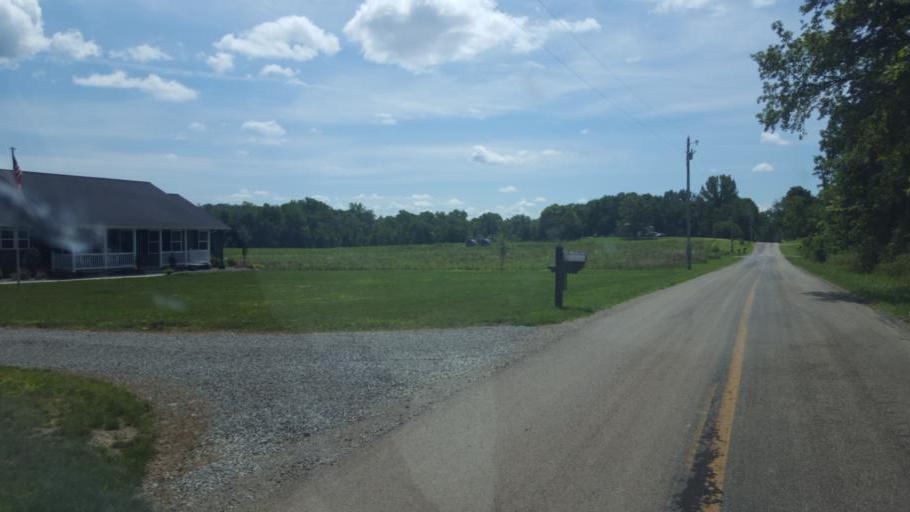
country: US
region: Ohio
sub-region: Delaware County
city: Sunbury
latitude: 40.3343
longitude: -82.8229
